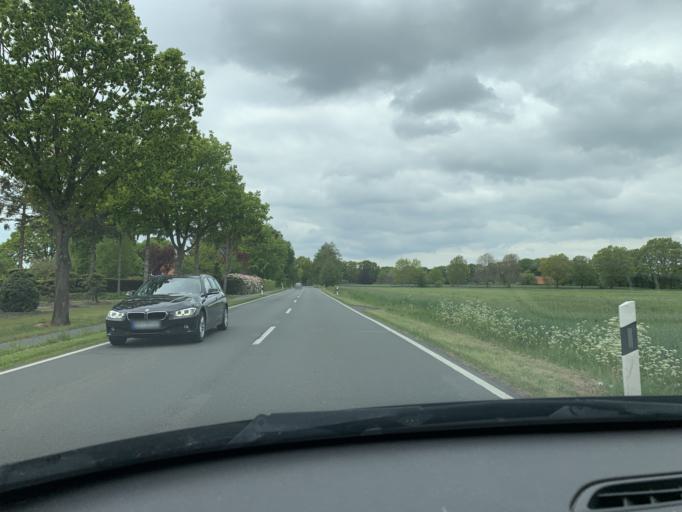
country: DE
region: Lower Saxony
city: Bad Zwischenahn
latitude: 53.1888
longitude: 8.0590
